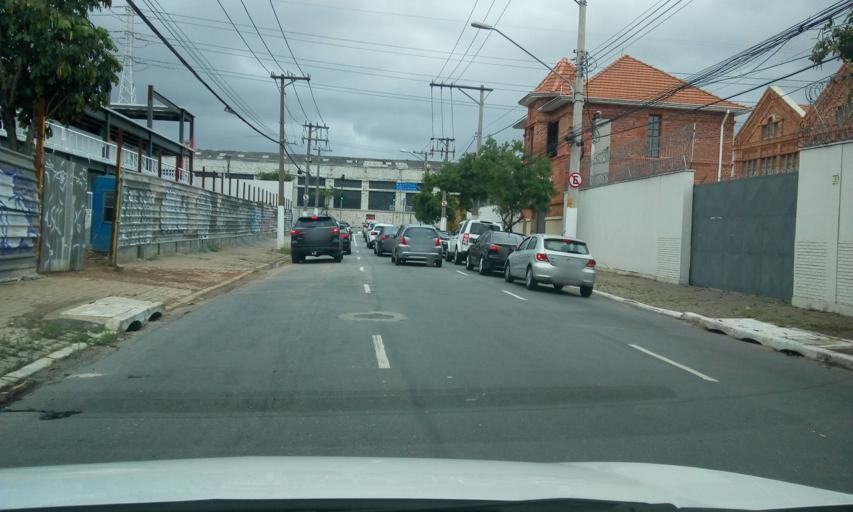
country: BR
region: Sao Paulo
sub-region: Sao Paulo
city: Sao Paulo
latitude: -23.5659
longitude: -46.6033
